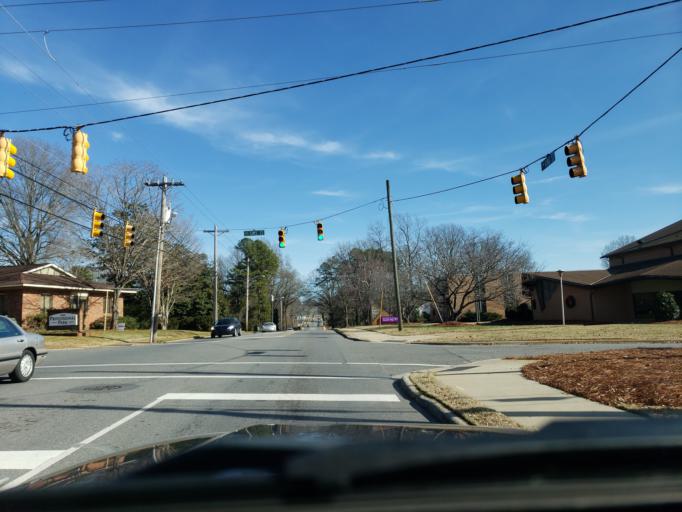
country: US
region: North Carolina
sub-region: Cleveland County
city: Kings Mountain
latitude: 35.2409
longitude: -81.3551
